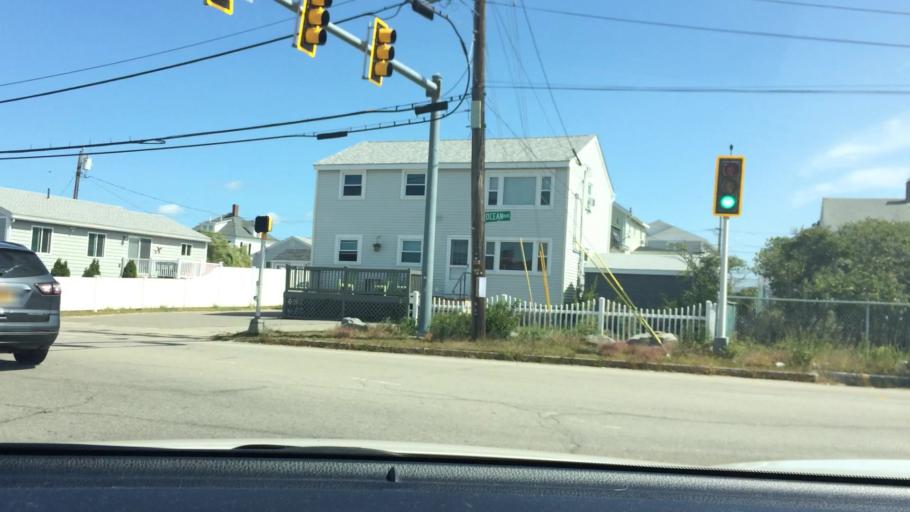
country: US
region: New Hampshire
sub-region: Rockingham County
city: Hampton Beach
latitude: 42.8724
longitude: -70.8184
